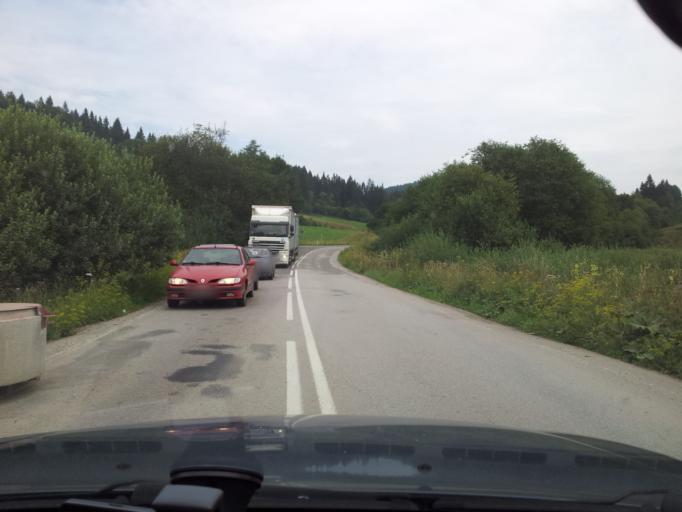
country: SK
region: Zilinsky
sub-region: Okres Dolny Kubin
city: Dolny Kubin
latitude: 49.2811
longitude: 19.3470
